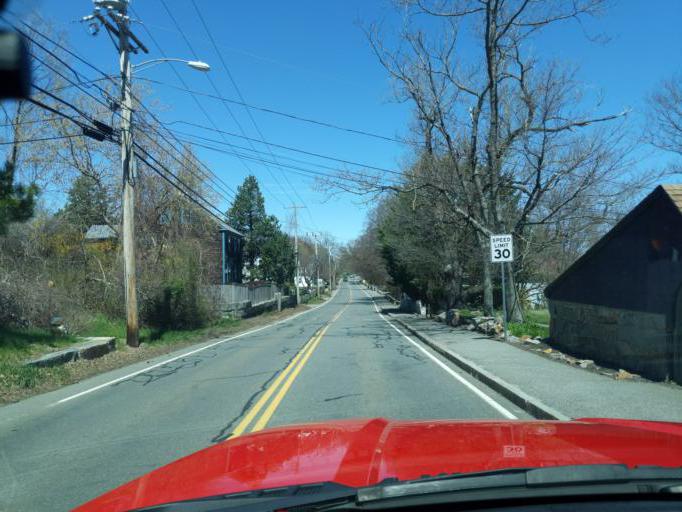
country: US
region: Massachusetts
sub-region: Essex County
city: Rockport
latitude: 42.6681
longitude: -70.6247
